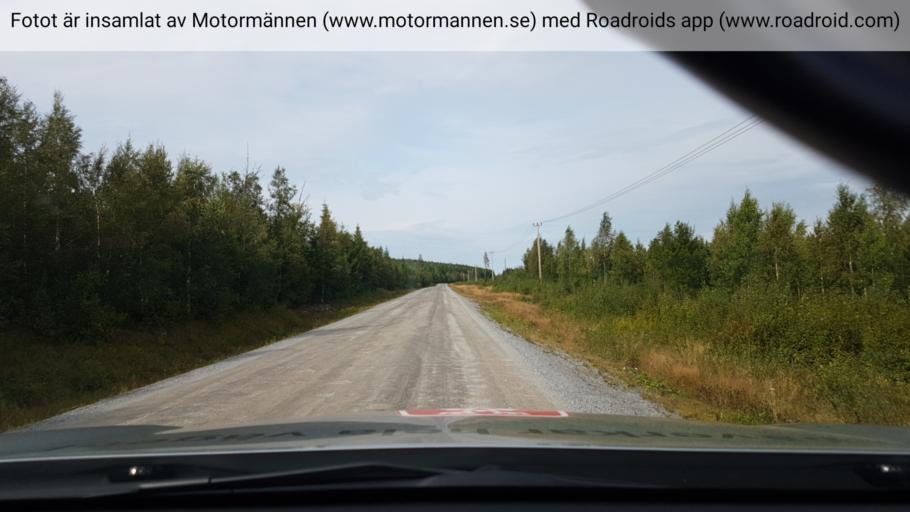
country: SE
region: Vaesterbotten
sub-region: Bjurholms Kommun
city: Bjurholm
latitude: 63.8863
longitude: 19.4281
